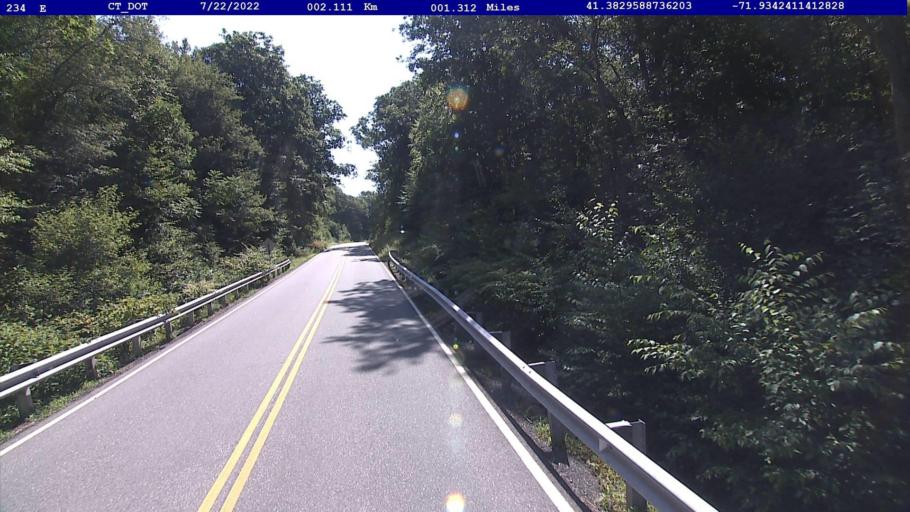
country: US
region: Connecticut
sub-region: New London County
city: Old Mystic
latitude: 41.3829
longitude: -71.9342
